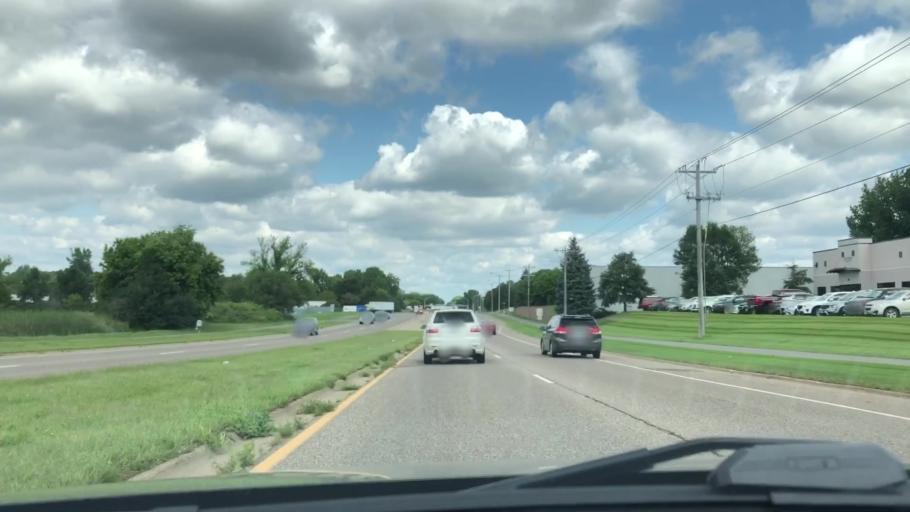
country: US
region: Minnesota
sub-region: Dakota County
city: Eagan
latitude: 44.8398
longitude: -93.1468
